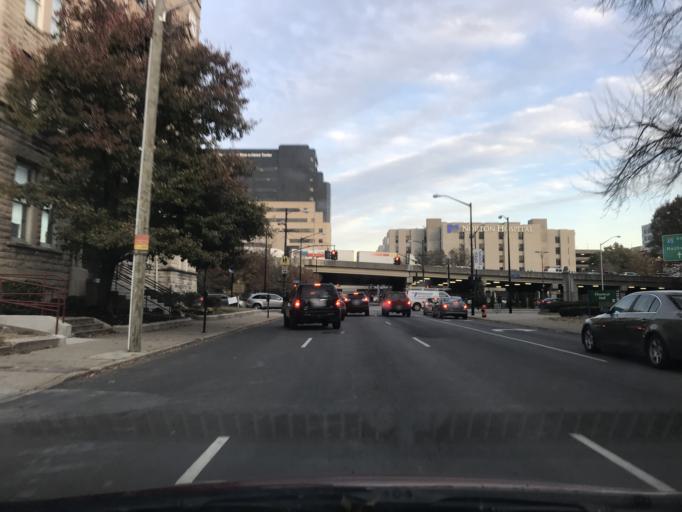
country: US
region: Kentucky
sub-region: Jefferson County
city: Louisville
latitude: 38.2485
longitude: -85.7536
